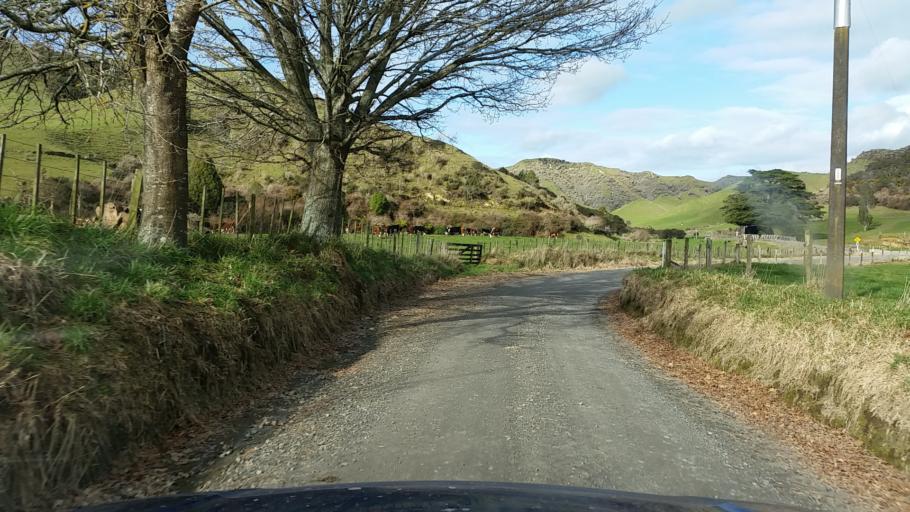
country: NZ
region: Taranaki
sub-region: South Taranaki District
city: Eltham
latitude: -39.2578
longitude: 174.5745
